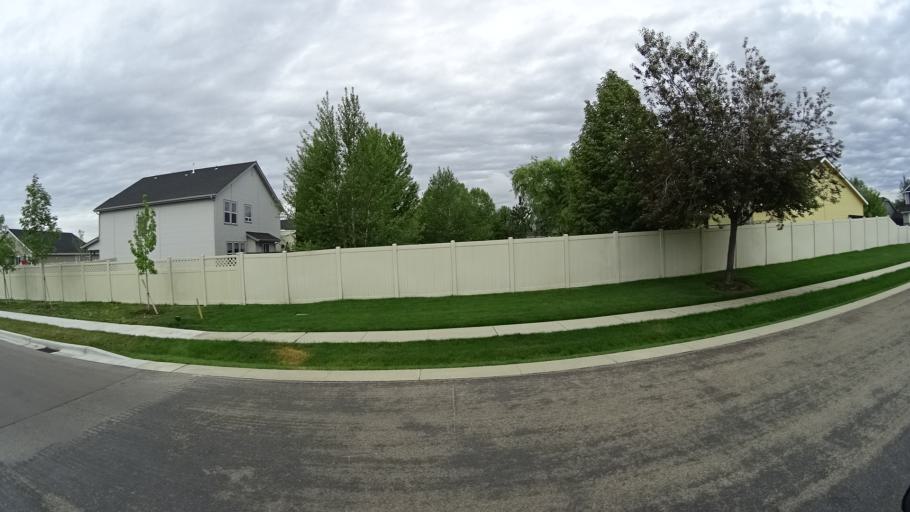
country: US
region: Idaho
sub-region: Ada County
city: Star
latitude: 43.7010
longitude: -116.5056
